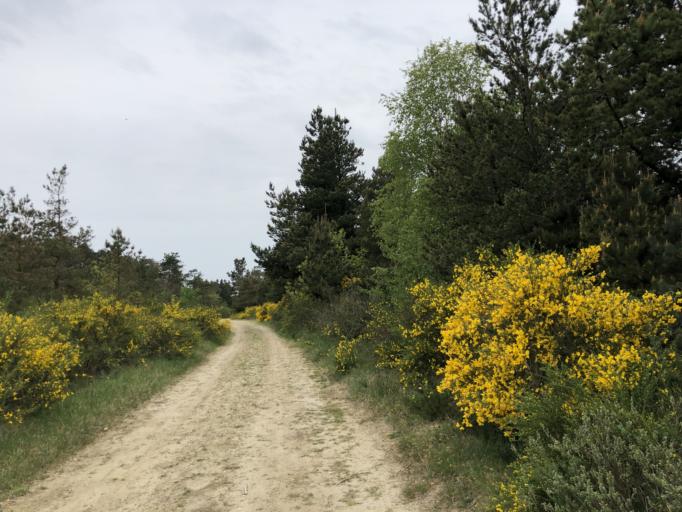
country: DK
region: Central Jutland
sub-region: Holstebro Kommune
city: Ulfborg
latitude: 56.2813
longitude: 8.4007
